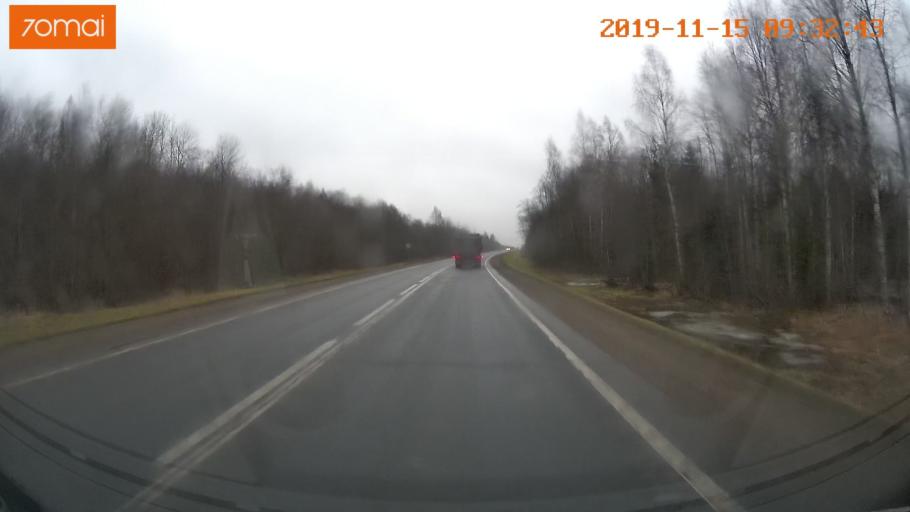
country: RU
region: Vologda
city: Sheksna
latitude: 59.2704
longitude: 38.3419
